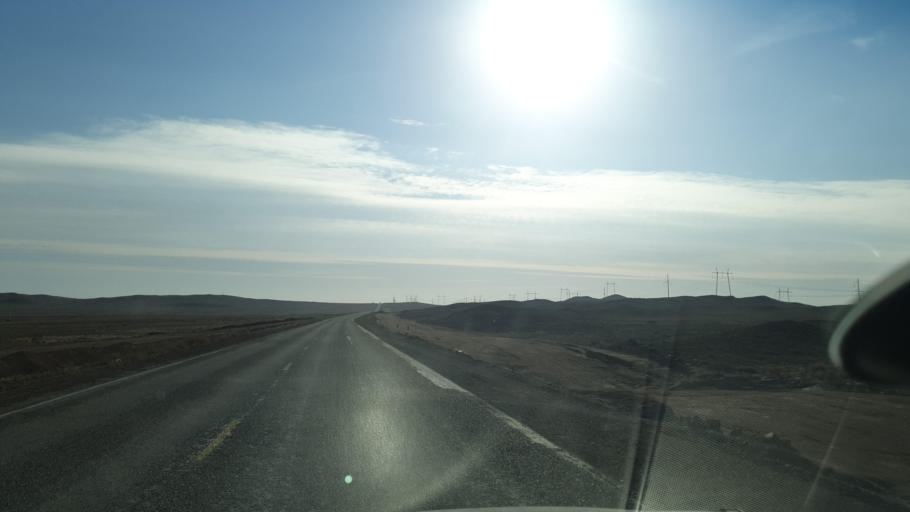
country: KZ
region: Zhambyl
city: Mynaral
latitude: 45.6826
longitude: 73.4012
